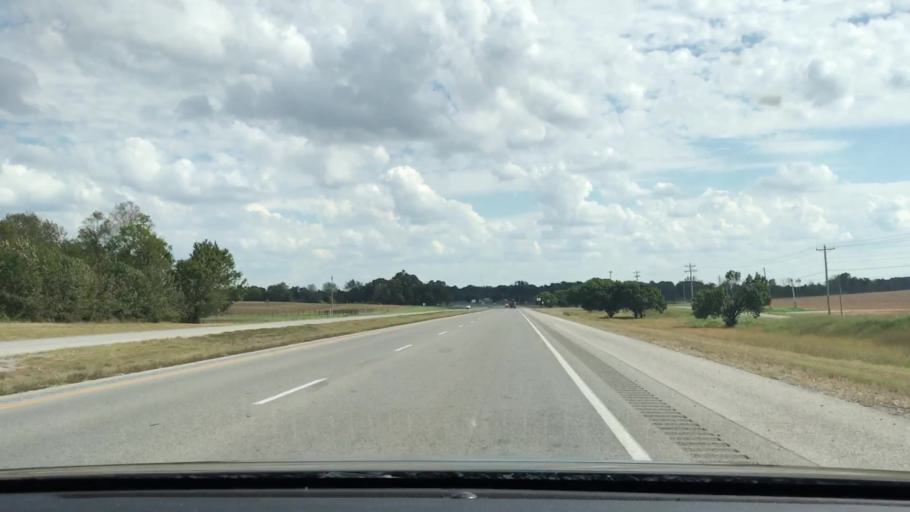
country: US
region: Kentucky
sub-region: Trigg County
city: Cadiz
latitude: 36.8678
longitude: -87.7866
